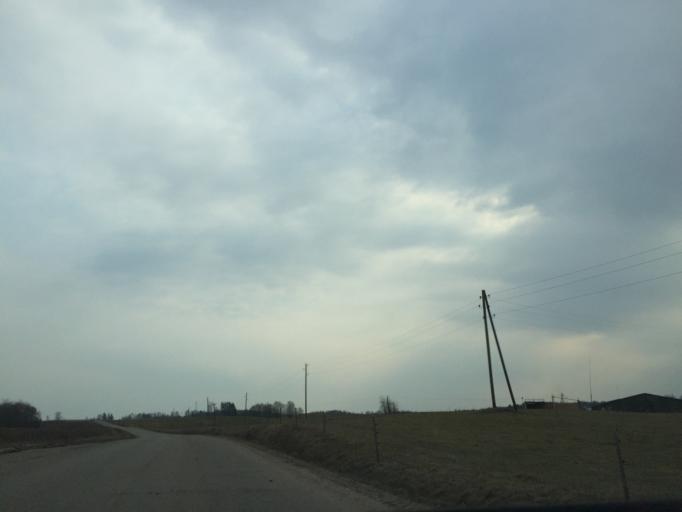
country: LV
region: Priekuli
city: Priekuli
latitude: 57.2445
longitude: 25.3726
